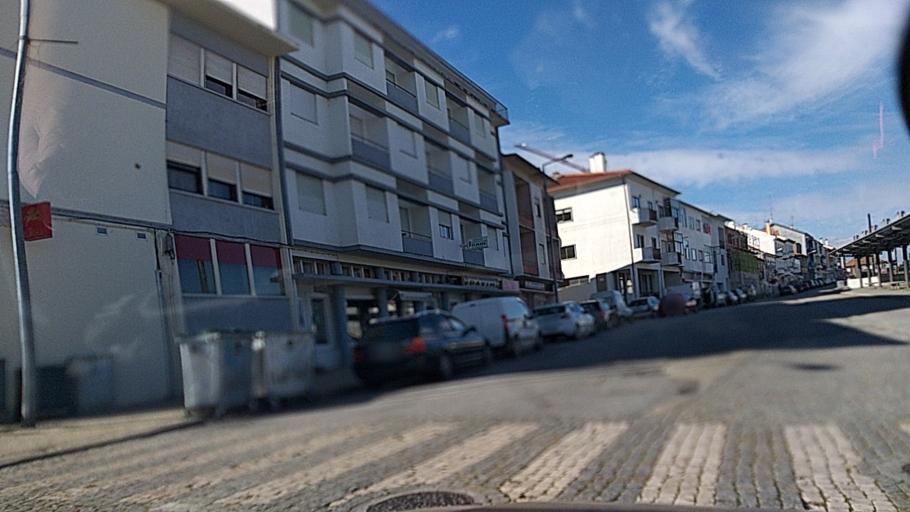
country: PT
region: Guarda
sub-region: Guarda
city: Sequeira
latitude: 40.5526
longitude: -7.2404
